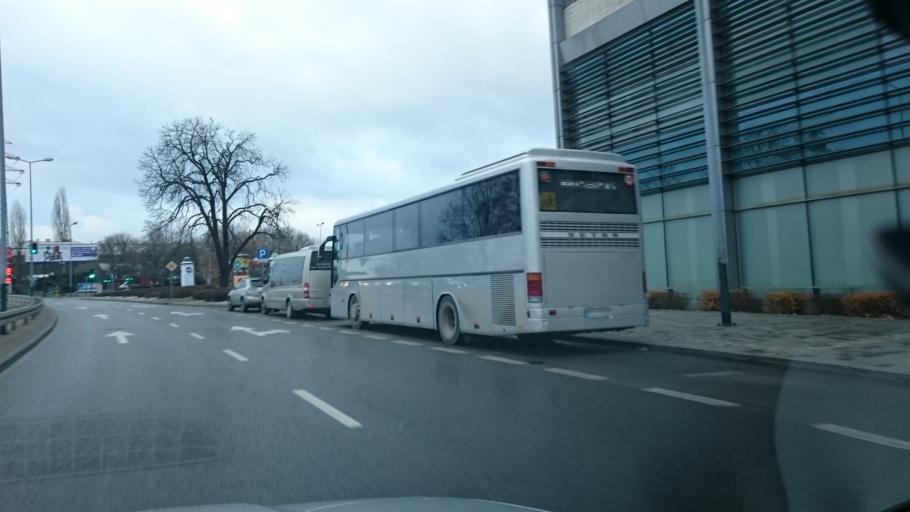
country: PL
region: Lesser Poland Voivodeship
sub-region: Krakow
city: Krakow
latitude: 50.0524
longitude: 19.9563
